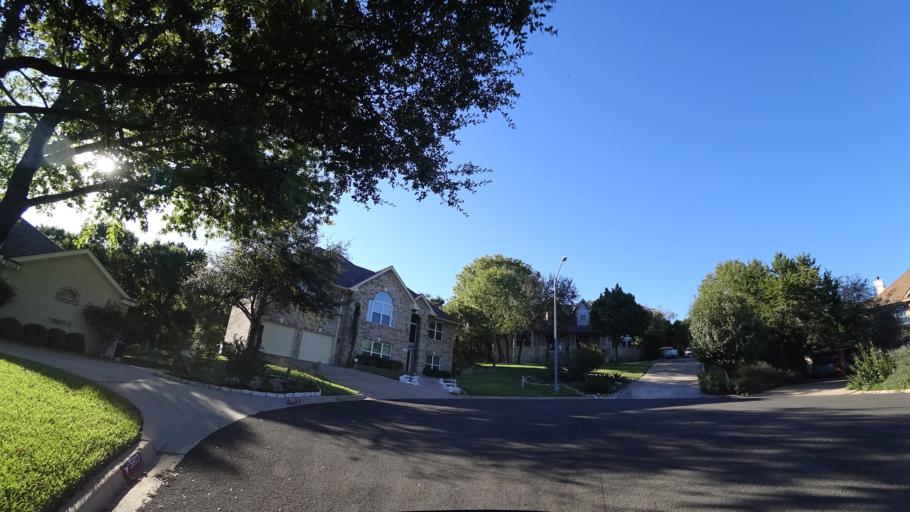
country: US
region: Texas
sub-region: Travis County
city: West Lake Hills
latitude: 30.3615
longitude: -97.8026
